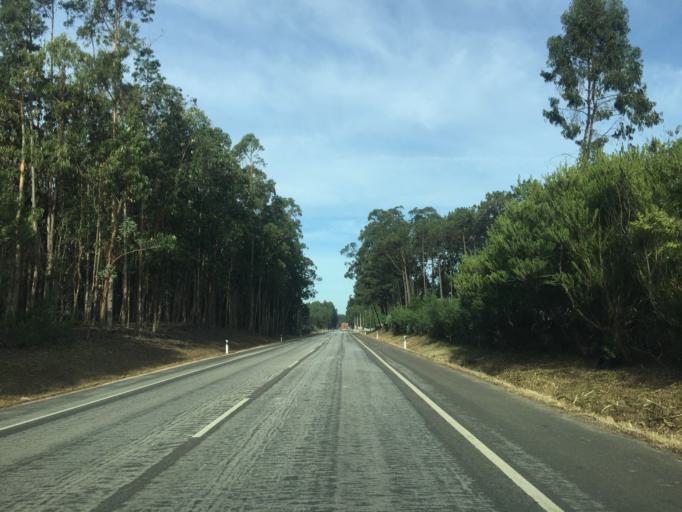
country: PT
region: Coimbra
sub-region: Figueira da Foz
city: Lavos
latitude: 40.0316
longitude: -8.8381
